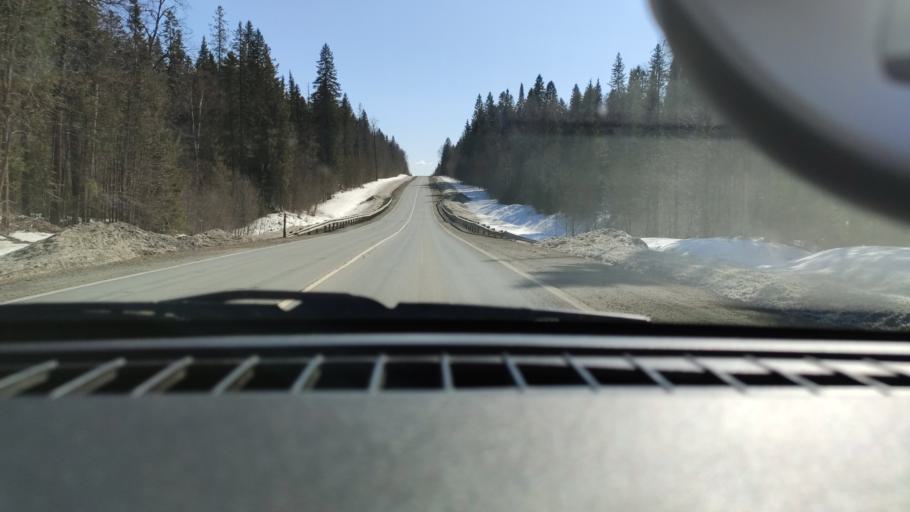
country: RU
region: Perm
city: Perm
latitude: 58.1920
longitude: 56.2139
